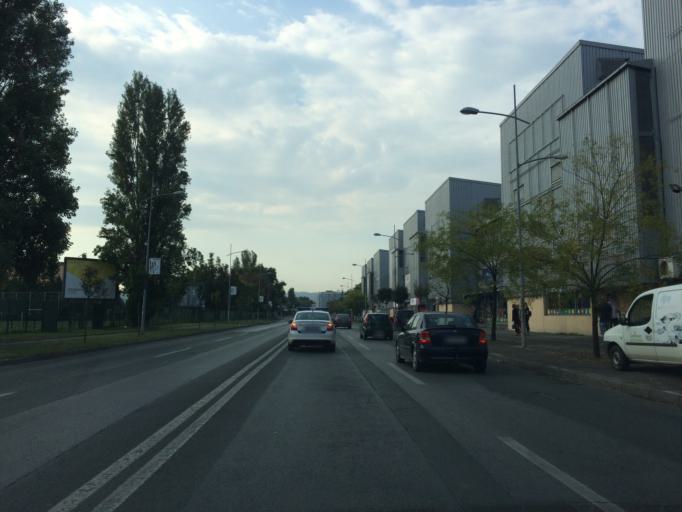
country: RS
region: Autonomna Pokrajina Vojvodina
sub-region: Juznobacki Okrug
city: Novi Sad
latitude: 45.2565
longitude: 19.8241
